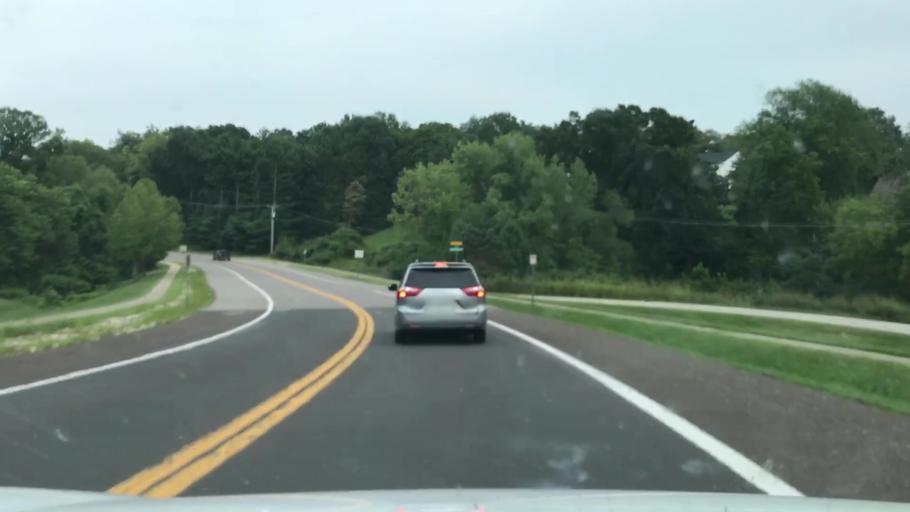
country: US
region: Missouri
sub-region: Saint Louis County
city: Clarkson Valley
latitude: 38.6239
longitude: -90.5902
